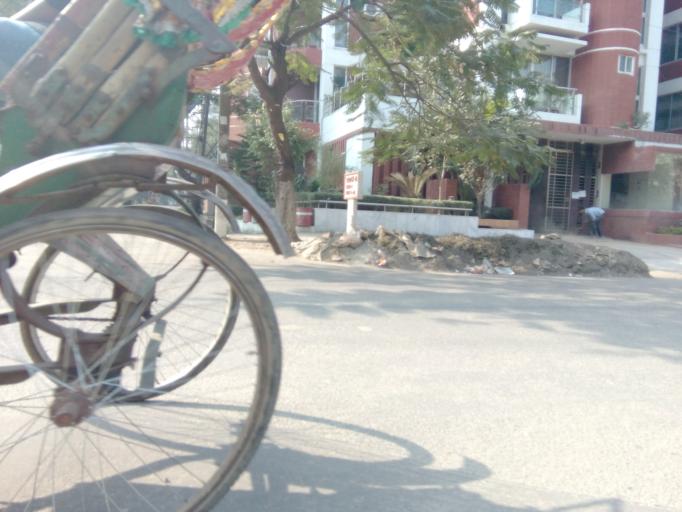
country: BD
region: Dhaka
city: Tungi
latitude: 23.8182
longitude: 90.4340
